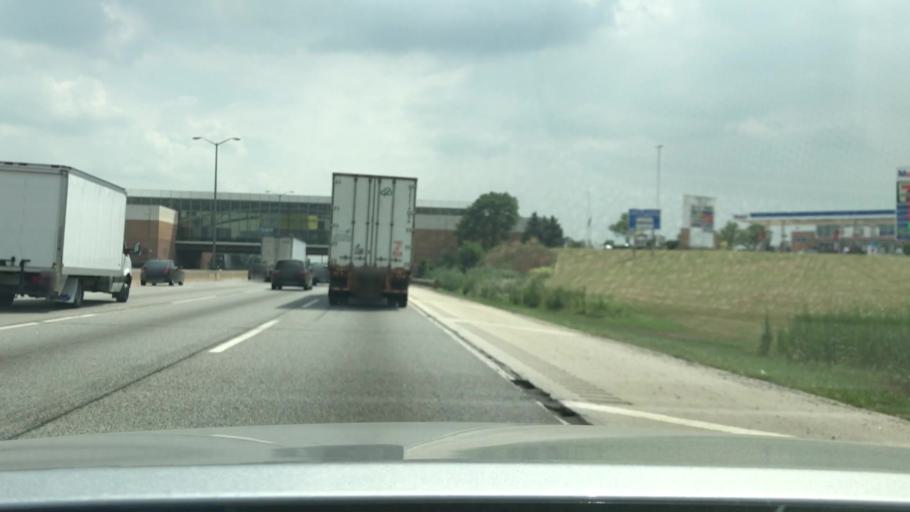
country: US
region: Illinois
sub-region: Cook County
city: Indian Head Park
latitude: 41.7851
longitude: -87.9082
